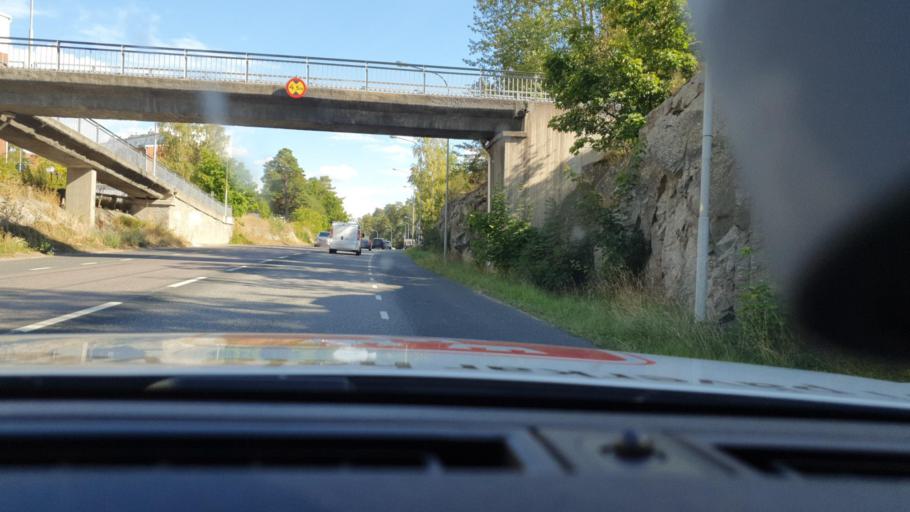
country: SE
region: Stockholm
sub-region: Vaxholms Kommun
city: Resaro
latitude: 59.4044
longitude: 18.3221
